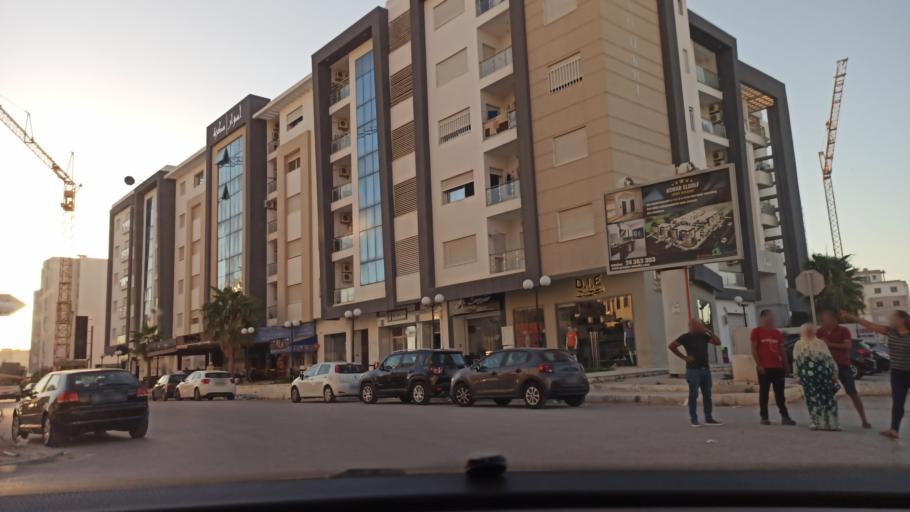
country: TN
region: Tunis
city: La Goulette
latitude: 36.8622
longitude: 10.2653
